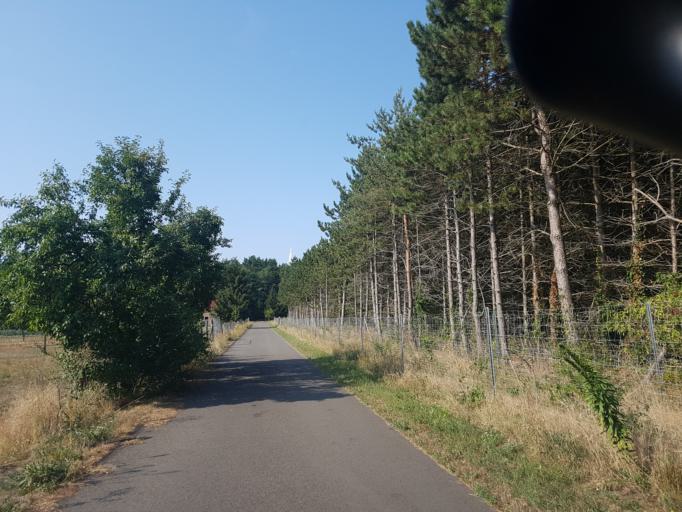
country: DE
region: Brandenburg
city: Niemegk
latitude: 52.0893
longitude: 12.7513
